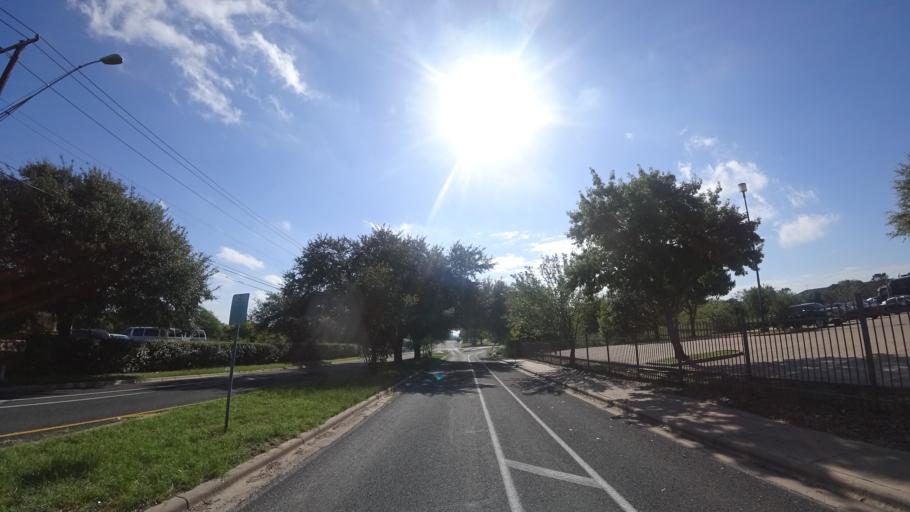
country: US
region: Texas
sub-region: Travis County
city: Austin
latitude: 30.3286
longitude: -97.7035
